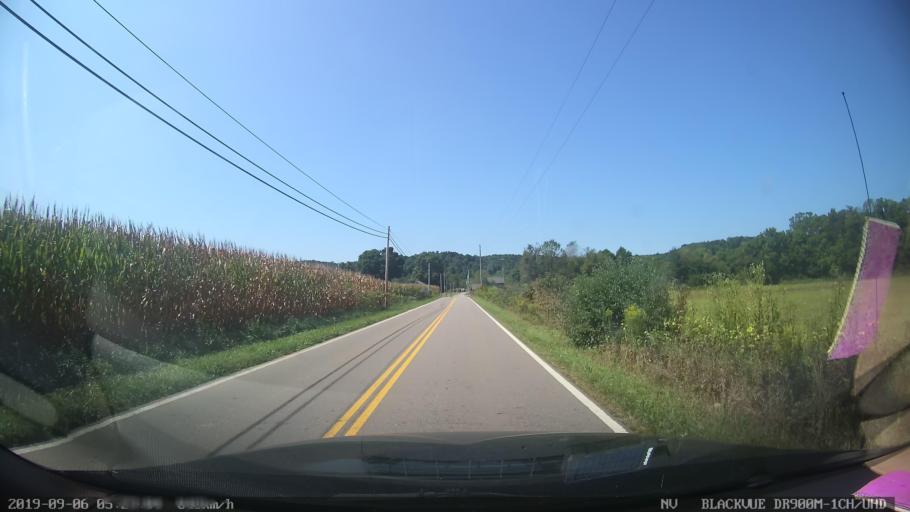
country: US
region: Ohio
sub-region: Licking County
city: Utica
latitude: 40.1782
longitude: -82.4145
